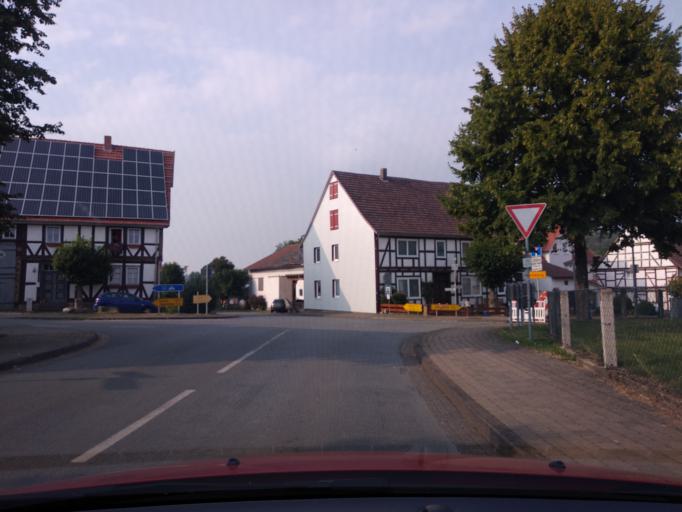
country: DE
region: Hesse
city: Liebenau
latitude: 51.4600
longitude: 9.3070
